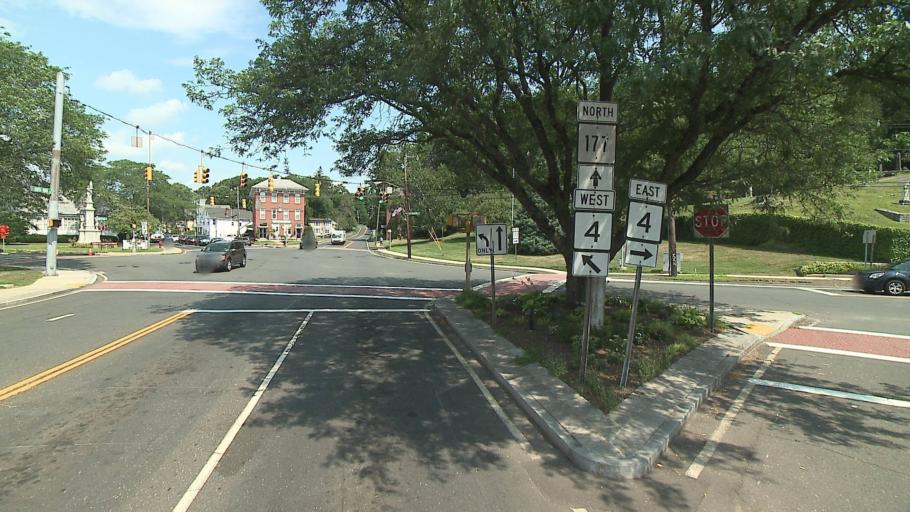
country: US
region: Connecticut
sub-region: Hartford County
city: Collinsville
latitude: 41.7576
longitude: -72.8869
